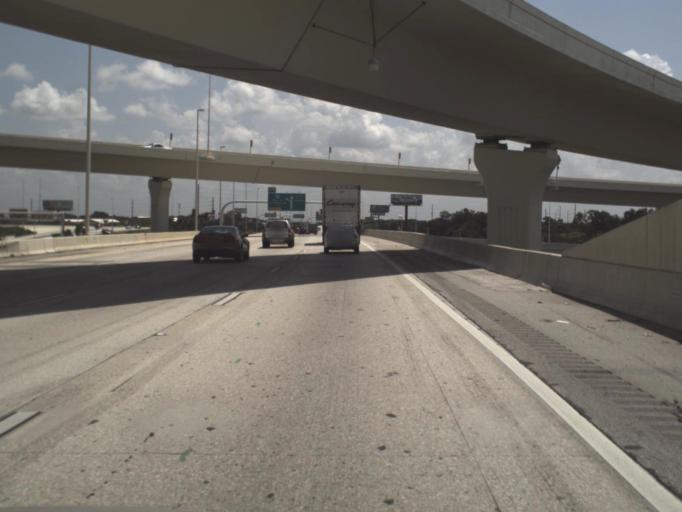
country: US
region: Florida
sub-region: Hillsborough County
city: Tampa
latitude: 27.9644
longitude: -82.4273
